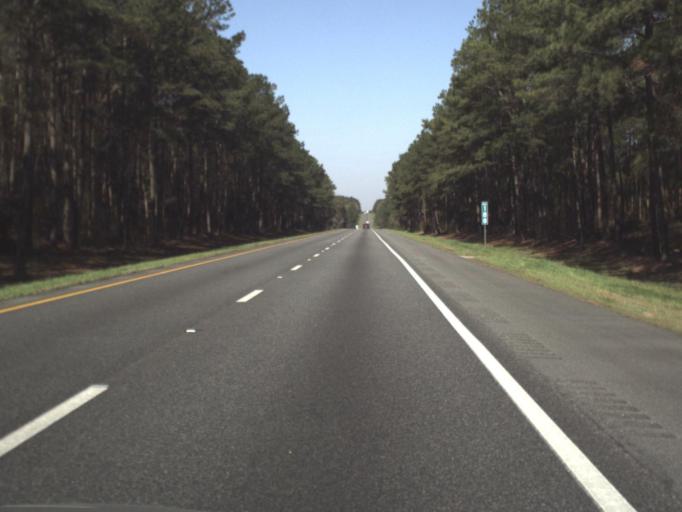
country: US
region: Florida
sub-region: Gadsden County
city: Midway
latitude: 30.5144
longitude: -84.4752
